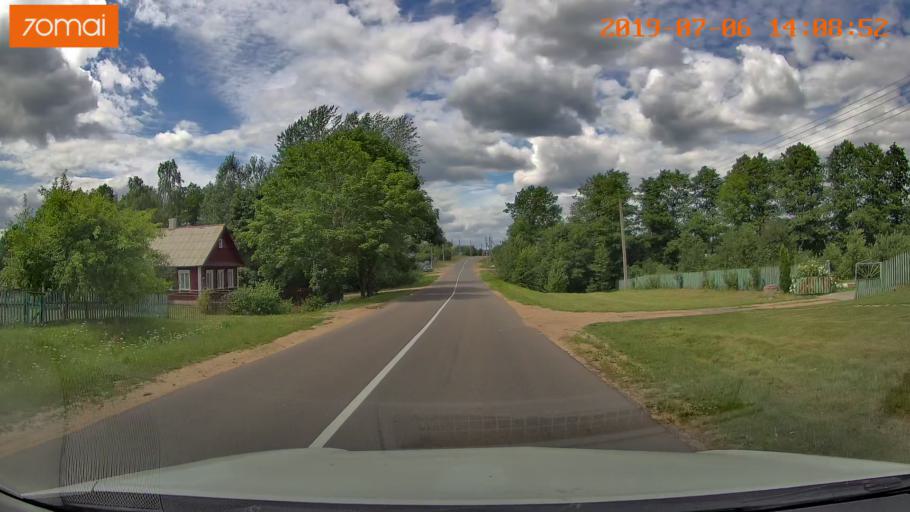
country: BY
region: Minsk
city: Ivyanyets
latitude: 53.8780
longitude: 26.7530
